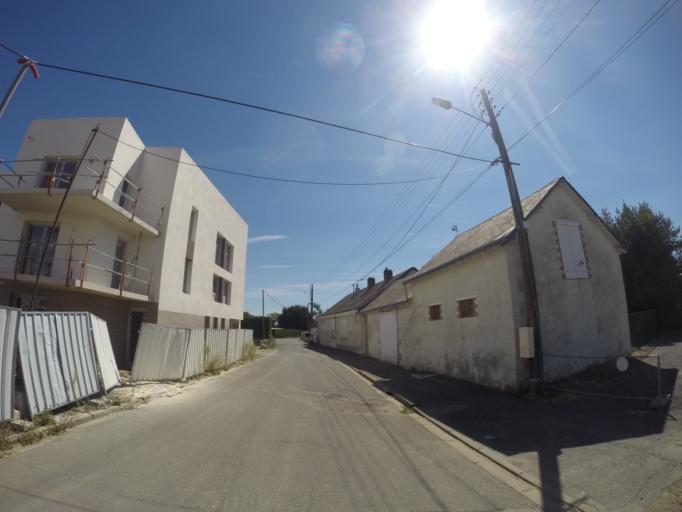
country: FR
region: Centre
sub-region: Departement d'Indre-et-Loire
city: Parcay-Meslay
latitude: 47.4219
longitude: 0.7100
